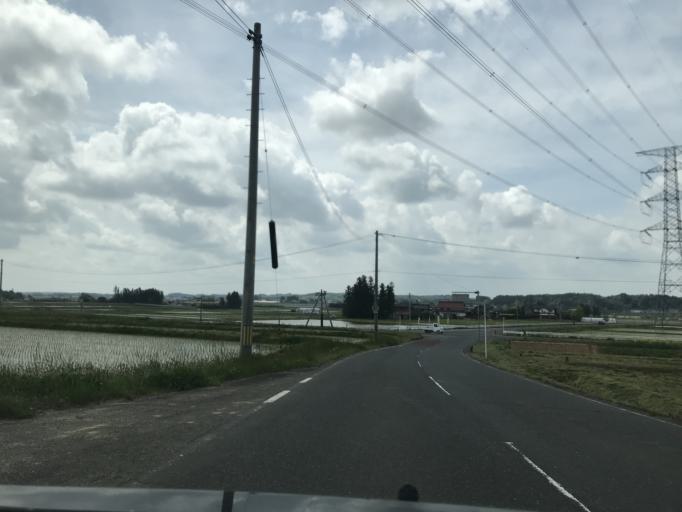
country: JP
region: Iwate
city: Ichinoseki
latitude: 38.8039
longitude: 141.0106
